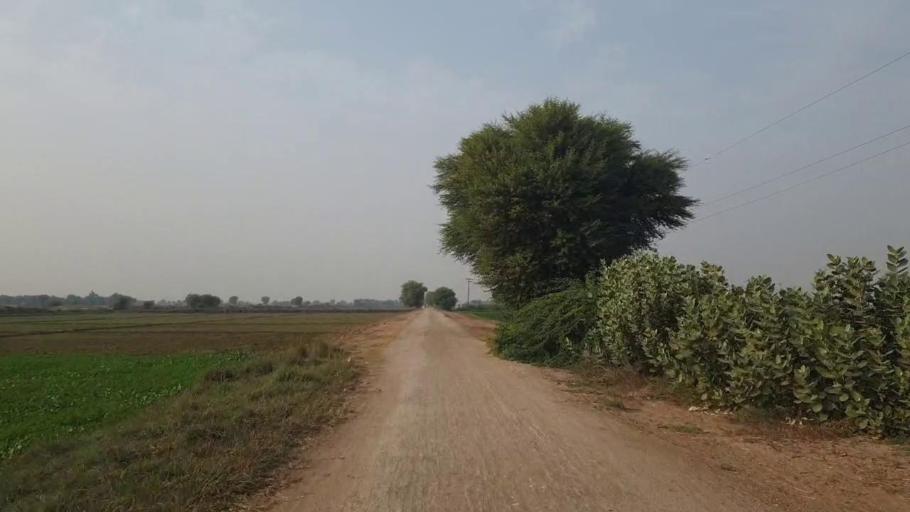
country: PK
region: Sindh
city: Sann
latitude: 26.0605
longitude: 68.1217
